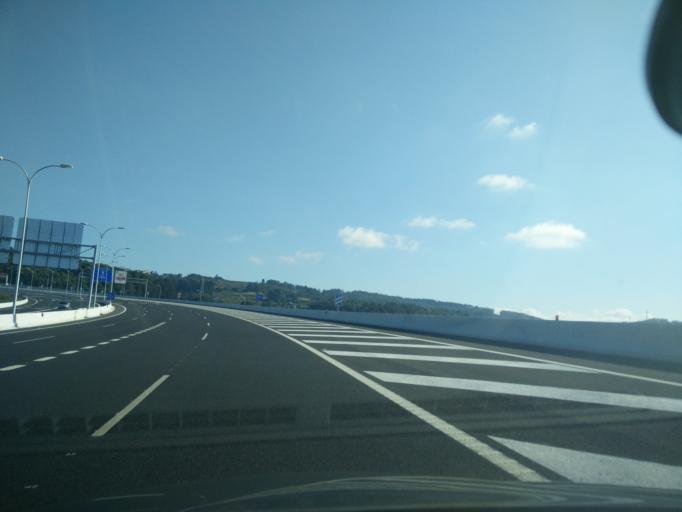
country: ES
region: Galicia
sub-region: Provincia da Coruna
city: A Coruna
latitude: 43.3288
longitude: -8.4236
